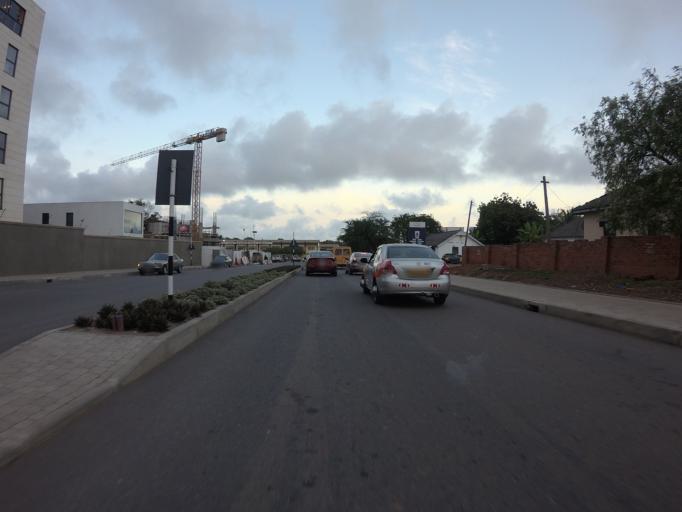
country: GH
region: Greater Accra
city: Accra
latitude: 5.5728
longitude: -0.1808
